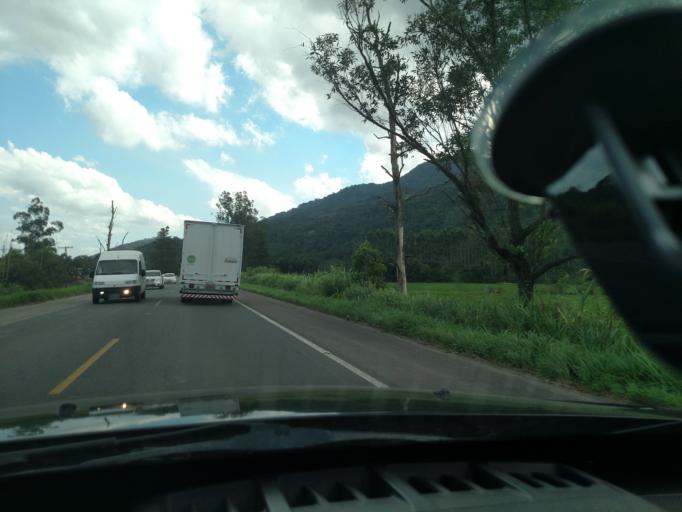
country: BR
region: Santa Catarina
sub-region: Indaial
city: Indaial
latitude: -26.9089
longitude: -49.2751
